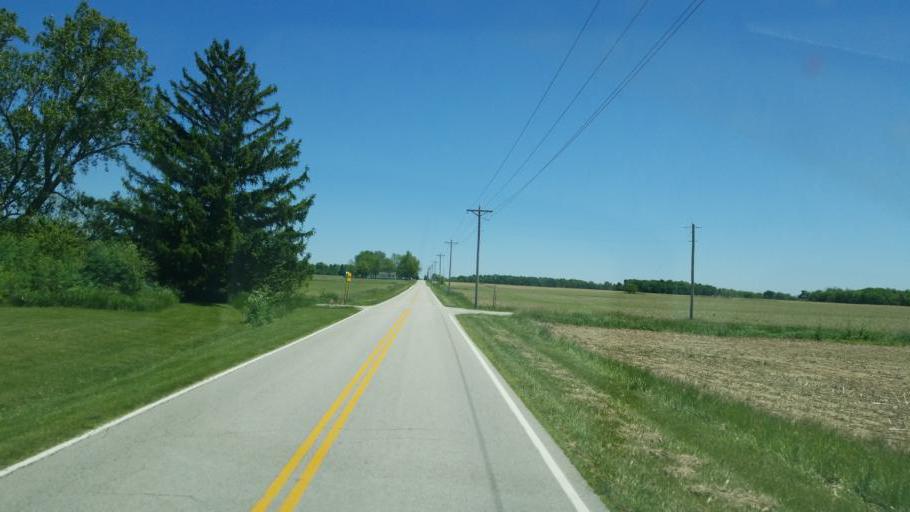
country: US
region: Ohio
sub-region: Darke County
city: Ansonia
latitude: 40.2648
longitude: -84.6666
